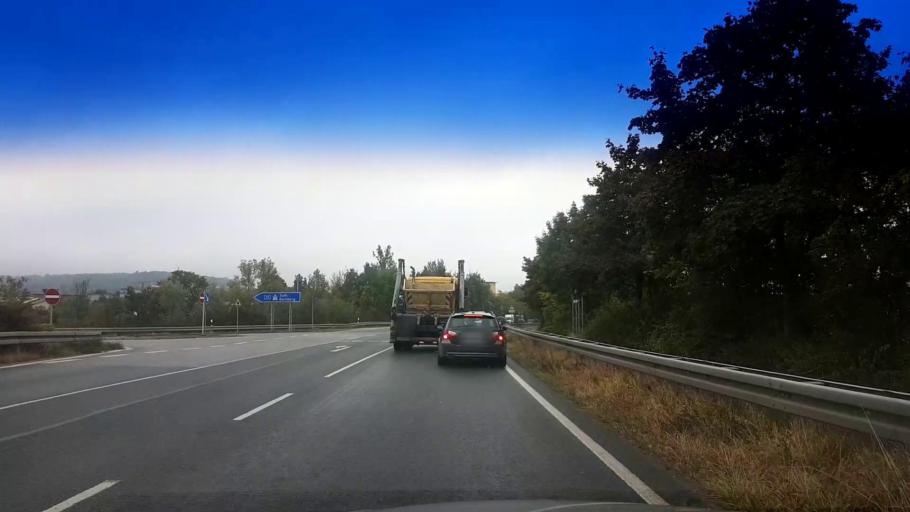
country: DE
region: Bavaria
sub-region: Upper Franconia
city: Forchheim
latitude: 49.7359
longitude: 11.0550
